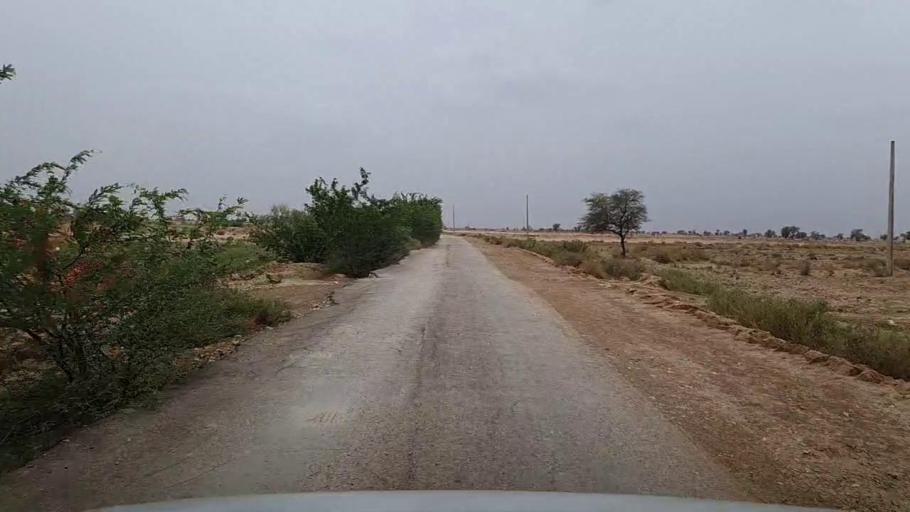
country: PK
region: Sindh
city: Sehwan
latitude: 26.3546
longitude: 67.7961
